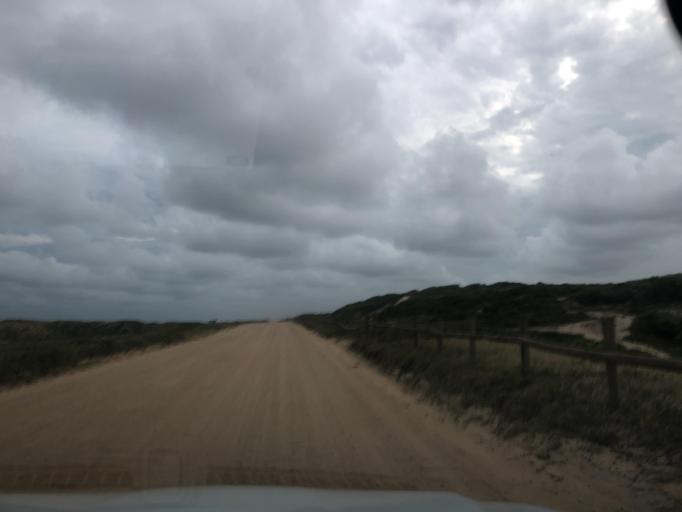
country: BR
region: Santa Catarina
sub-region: Sao Francisco Do Sul
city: Sao Francisco do Sul
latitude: -26.2492
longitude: -48.5123
